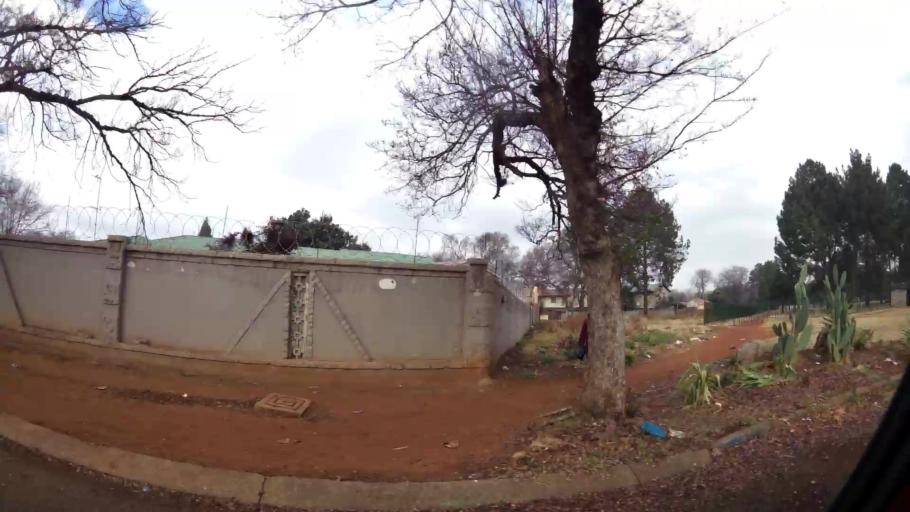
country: ZA
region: Gauteng
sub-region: Sedibeng District Municipality
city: Vanderbijlpark
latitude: -26.7002
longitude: 27.8299
